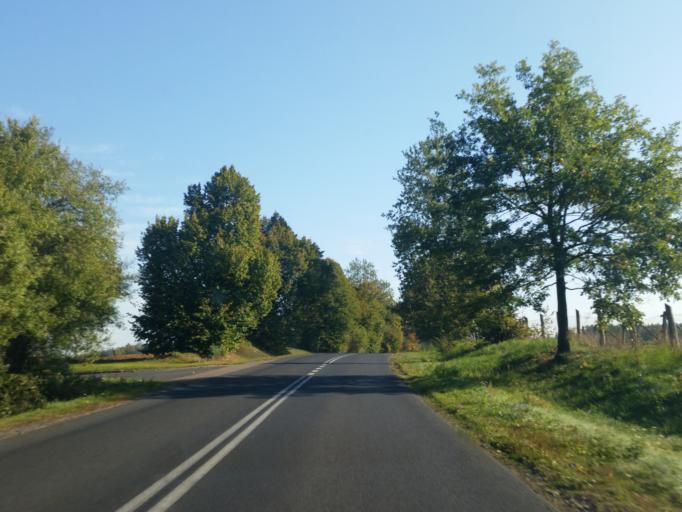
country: PL
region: Kujawsko-Pomorskie
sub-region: Powiat rypinski
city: Rypin
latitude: 53.0215
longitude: 19.4771
